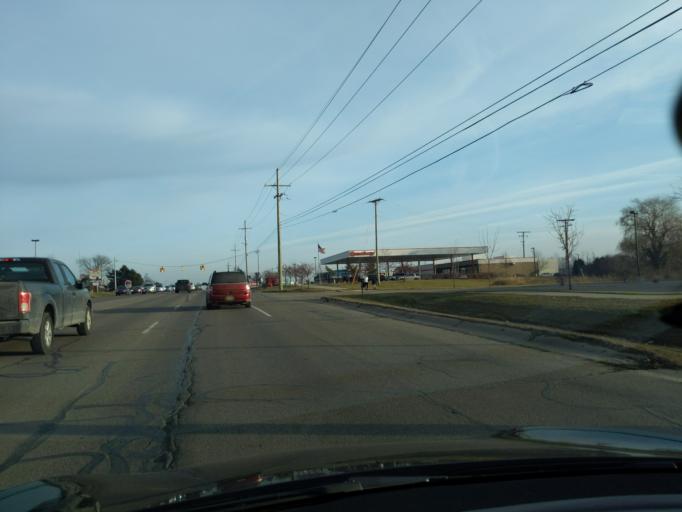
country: US
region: Michigan
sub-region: Livingston County
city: Howell
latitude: 42.5900
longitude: -83.8831
